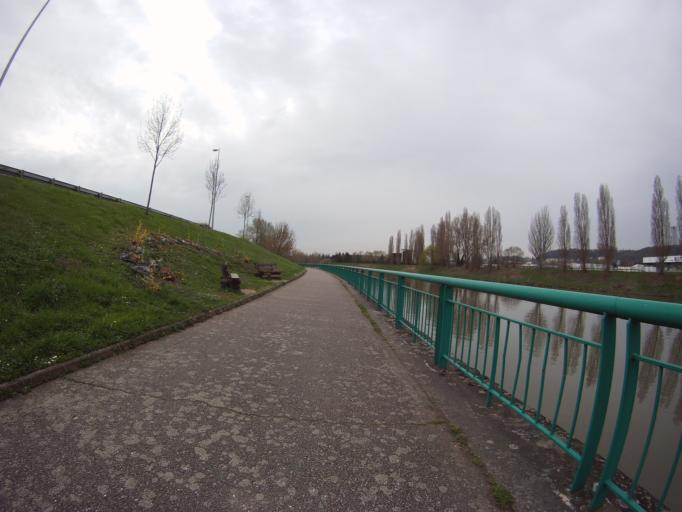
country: FR
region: Lorraine
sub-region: Departement de Meurthe-et-Moselle
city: Malzeville
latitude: 48.7155
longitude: 6.1745
